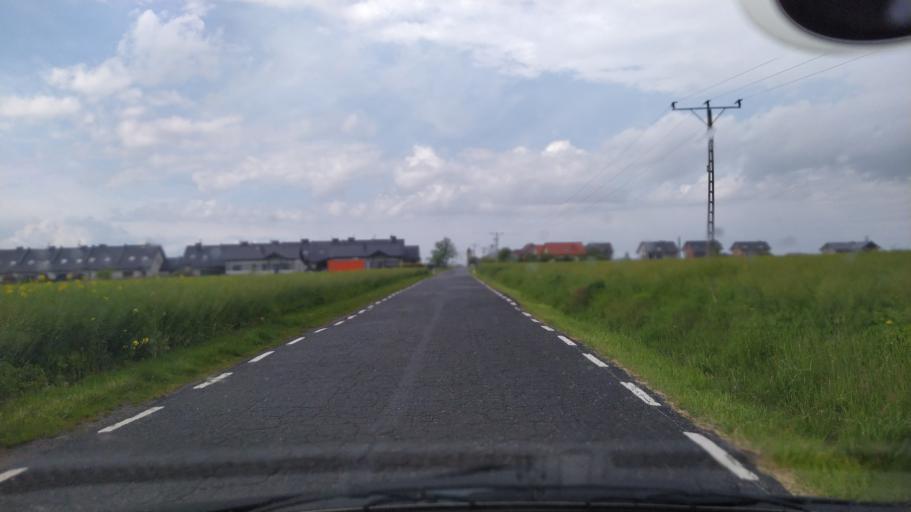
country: PL
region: Silesian Voivodeship
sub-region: Powiat gliwicki
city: Zernica
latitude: 50.2336
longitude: 18.6172
